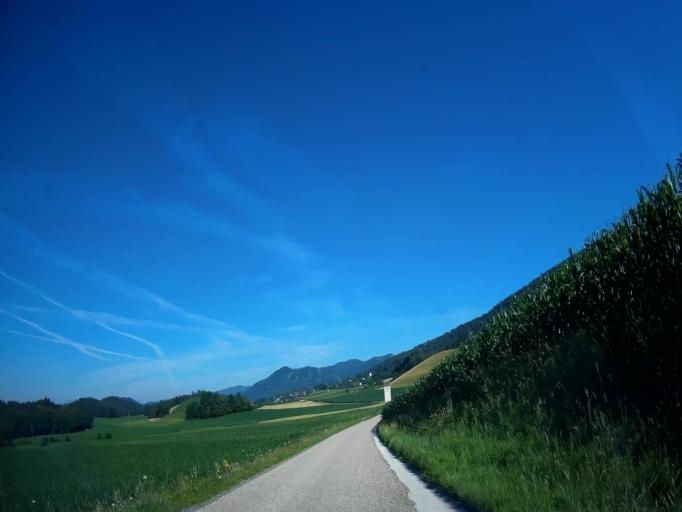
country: AT
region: Carinthia
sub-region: Politischer Bezirk Klagenfurt Land
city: Poggersdorf
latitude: 46.6692
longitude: 14.5304
